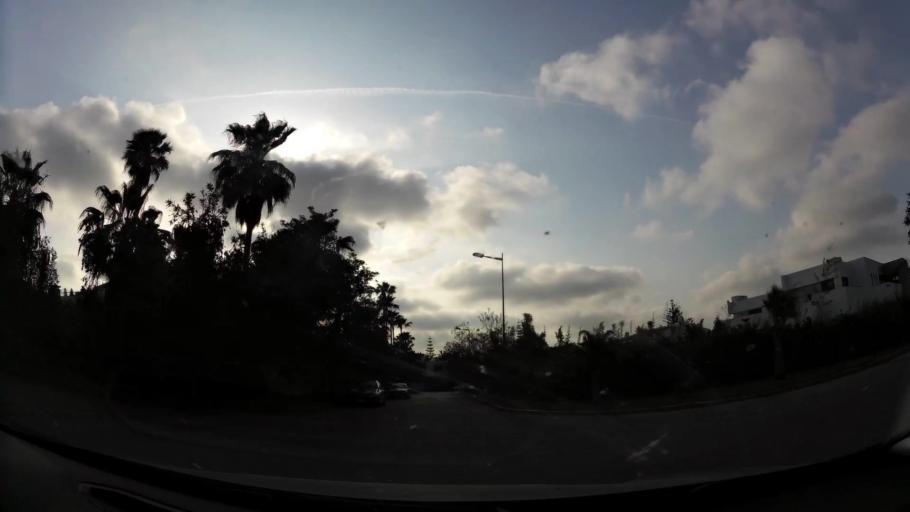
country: MA
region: Rabat-Sale-Zemmour-Zaer
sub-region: Rabat
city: Rabat
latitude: 33.9470
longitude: -6.8165
